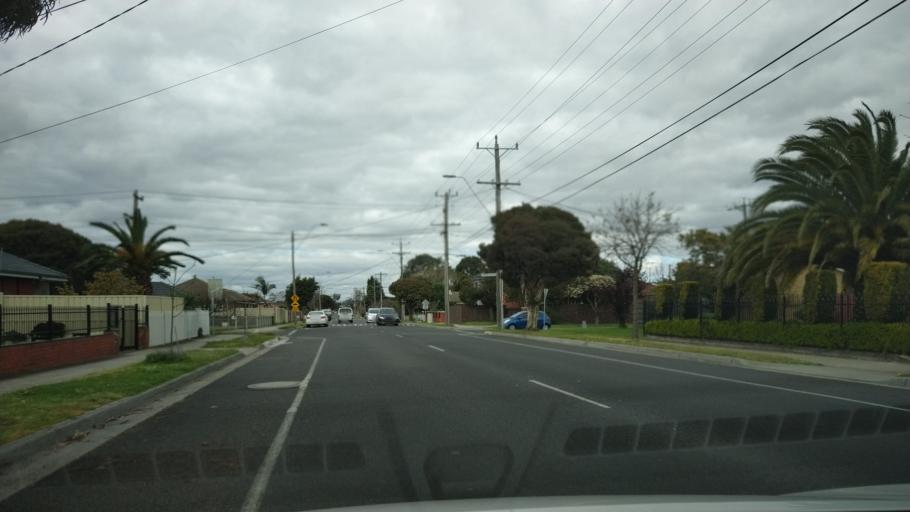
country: AU
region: Victoria
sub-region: Greater Dandenong
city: Springvale South
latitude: -37.9757
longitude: 145.1545
